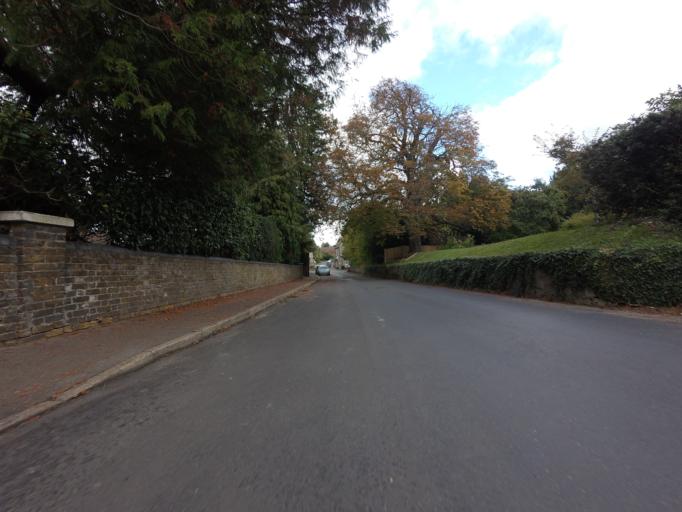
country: GB
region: England
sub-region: Kent
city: Swanley
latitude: 51.3827
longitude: 0.1621
